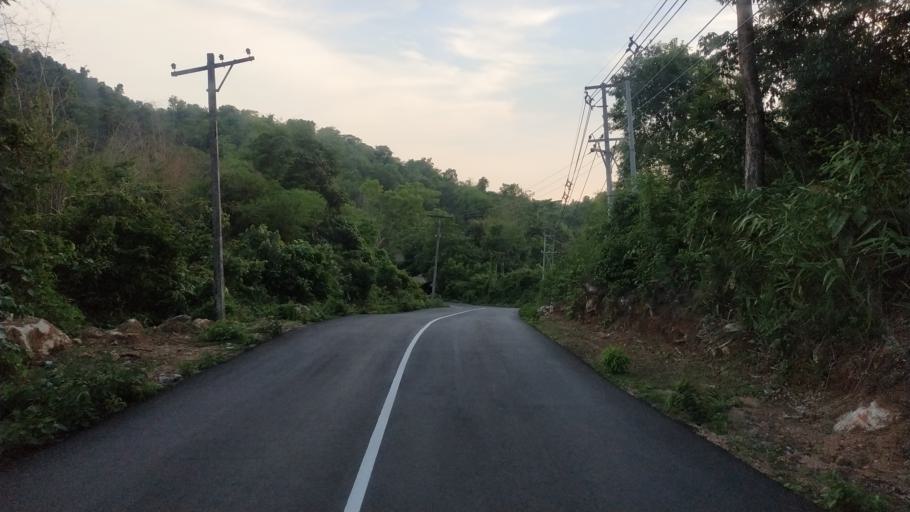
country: MM
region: Mon
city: Kyaikto
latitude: 17.4321
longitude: 97.0934
